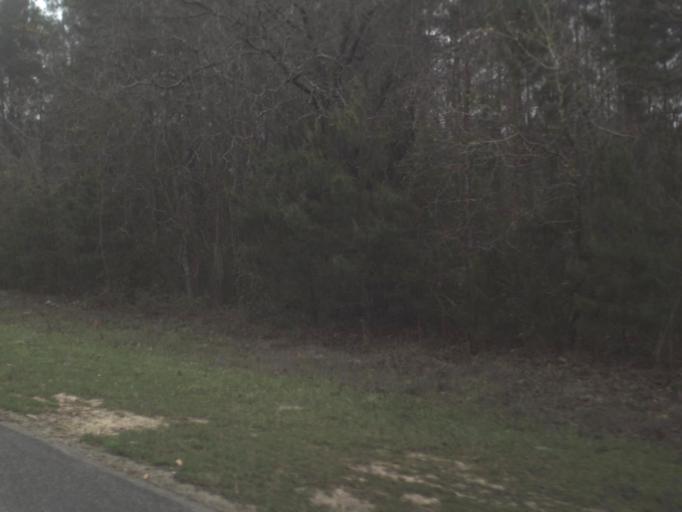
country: US
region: Florida
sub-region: Gadsden County
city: Gretna
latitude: 30.4770
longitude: -84.7287
